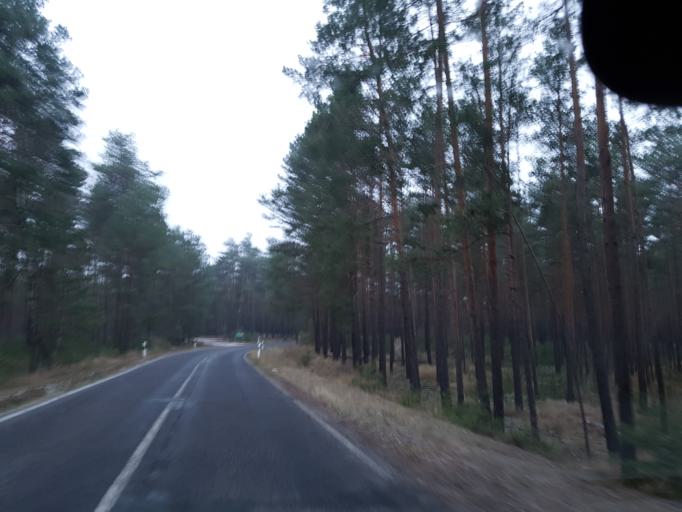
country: DE
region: Brandenburg
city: Finsterwalde
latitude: 51.6266
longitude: 13.6457
